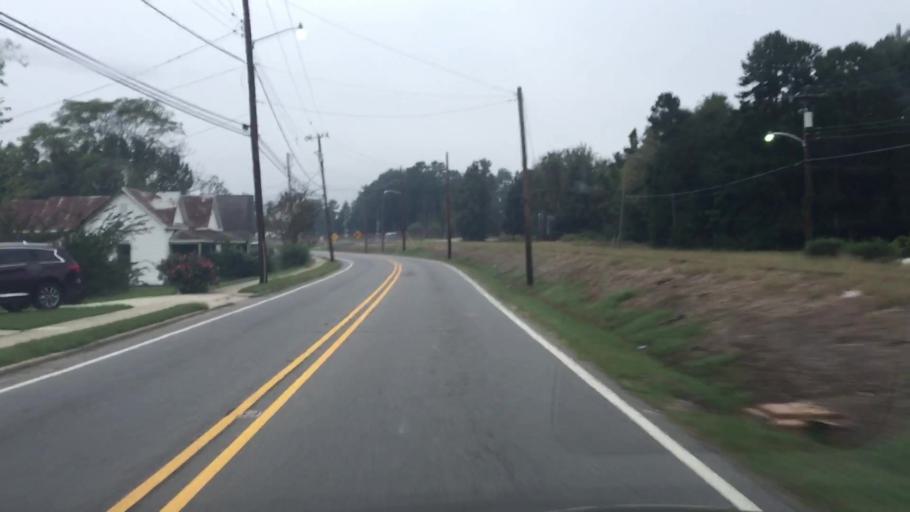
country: US
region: North Carolina
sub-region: Iredell County
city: Mooresville
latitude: 35.5958
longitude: -80.8078
